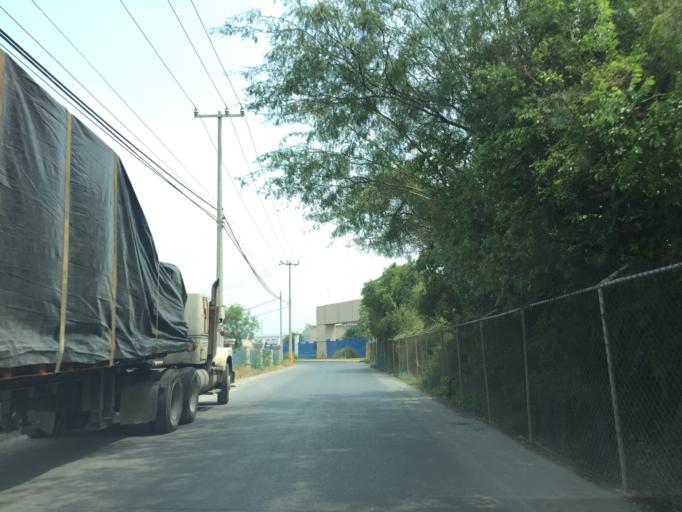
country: MX
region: Nuevo Leon
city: Apodaca
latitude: 25.7637
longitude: -100.1976
